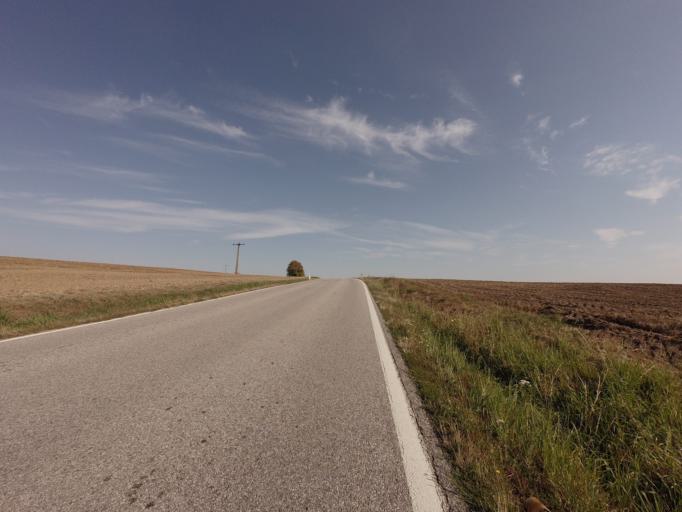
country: CZ
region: Jihocesky
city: Tyn nad Vltavou
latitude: 49.2862
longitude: 14.3957
